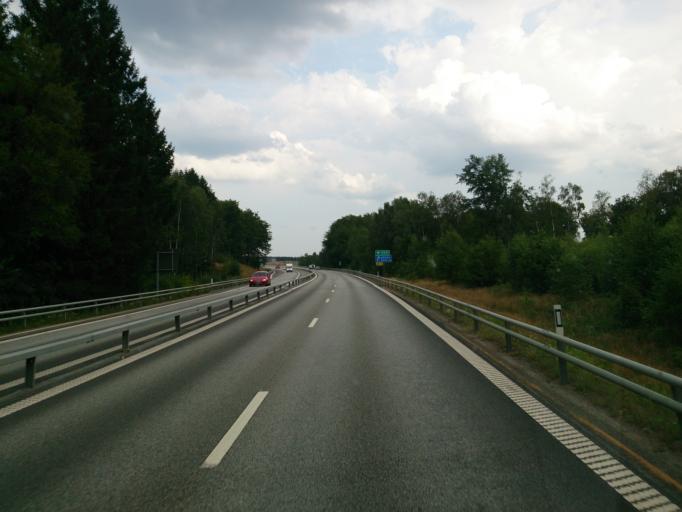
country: SE
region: Skane
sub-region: Horby Kommun
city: Hoerby
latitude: 55.8638
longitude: 13.6798
